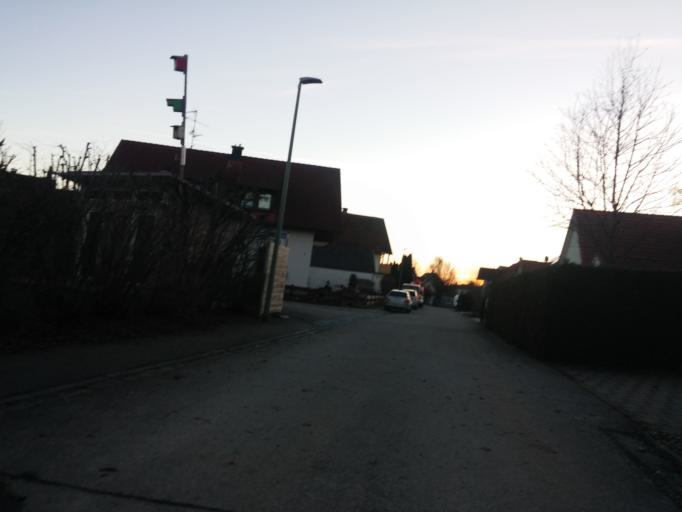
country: DE
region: Bavaria
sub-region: Swabia
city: Niederrieden
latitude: 48.0595
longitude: 10.1908
